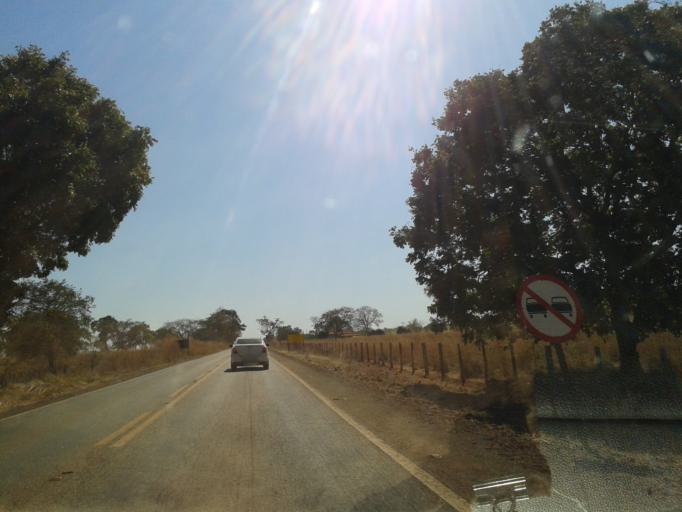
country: BR
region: Goias
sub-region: Crixas
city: Crixas
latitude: -14.1236
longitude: -50.3482
